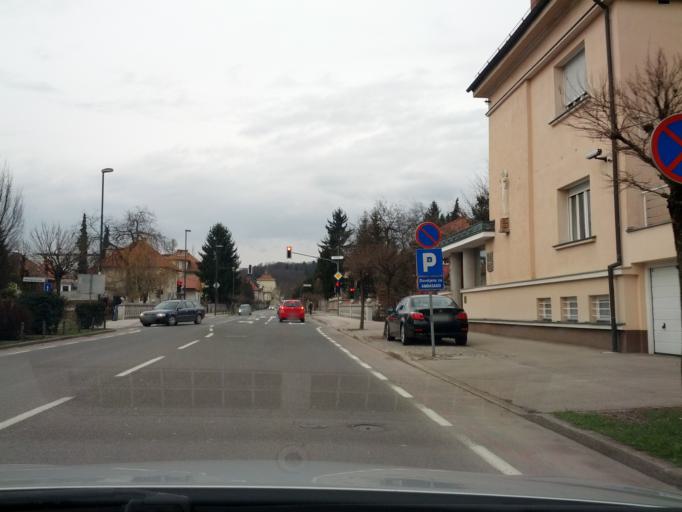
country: SI
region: Ljubljana
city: Ljubljana
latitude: 46.0432
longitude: 14.4980
